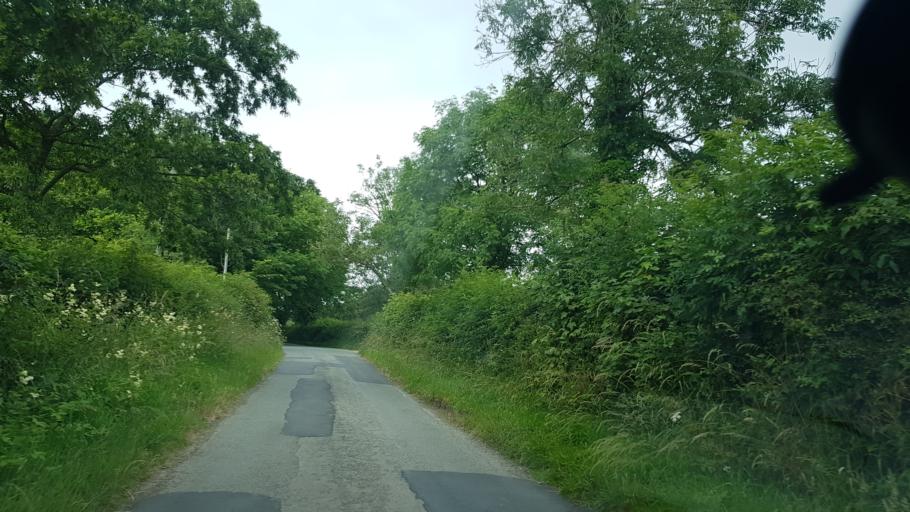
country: GB
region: Wales
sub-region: Pembrokeshire
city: Wiston
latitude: 51.7893
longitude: -4.8901
